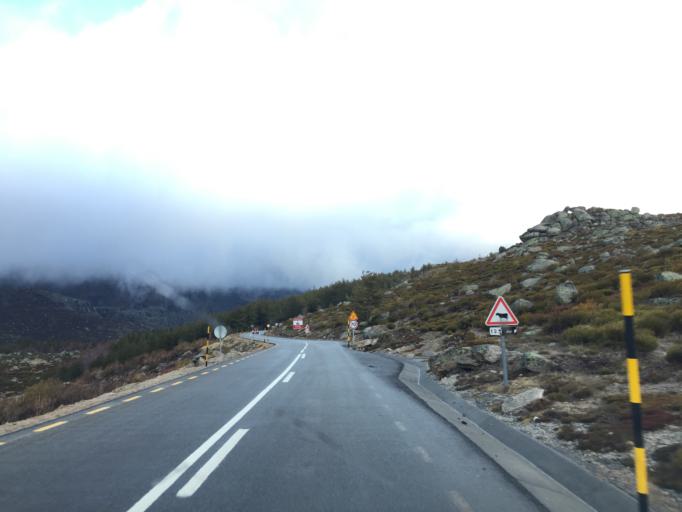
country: PT
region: Castelo Branco
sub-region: Covilha
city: Covilha
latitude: 40.3173
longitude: -7.5745
